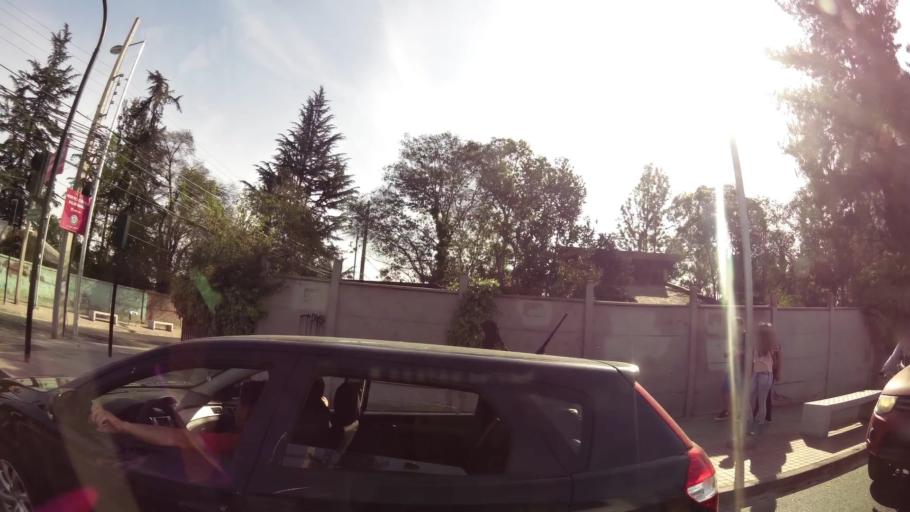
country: CL
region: Santiago Metropolitan
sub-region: Provincia de Santiago
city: Villa Presidente Frei, Nunoa, Santiago, Chile
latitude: -33.5263
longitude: -70.5890
